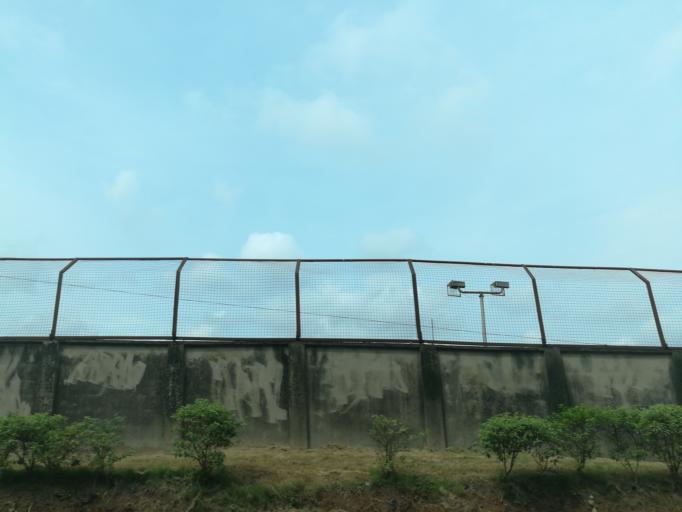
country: NG
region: Lagos
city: Ojota
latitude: 6.6070
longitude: 3.3698
